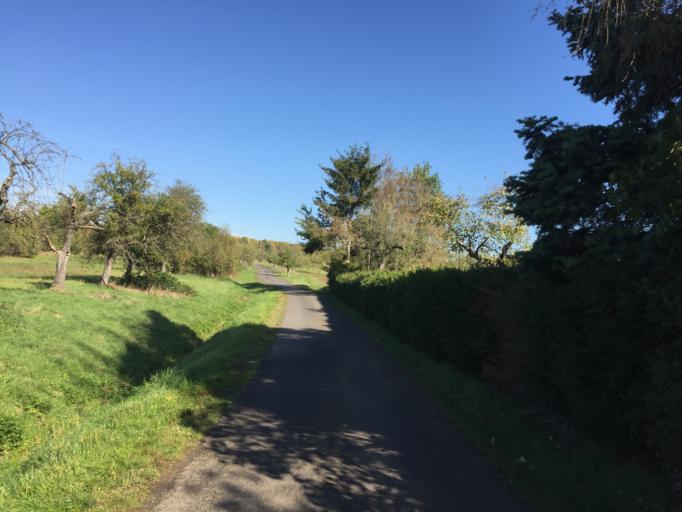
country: DE
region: Hesse
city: Lollar
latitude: 50.6186
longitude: 8.6936
